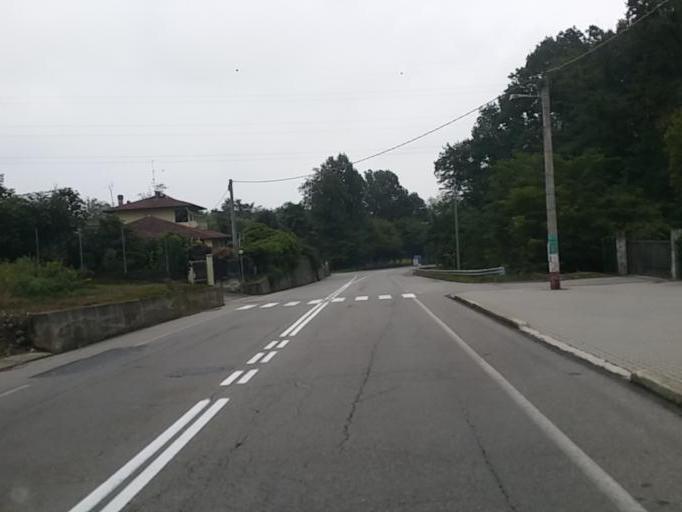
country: IT
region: Piedmont
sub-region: Provincia di Novara
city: Comignago
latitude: 45.7113
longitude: 8.5573
